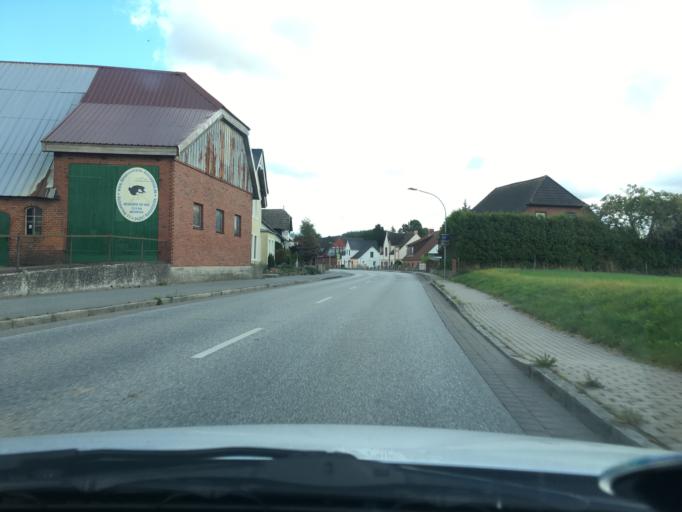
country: DE
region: Schleswig-Holstein
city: Barsbek
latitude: 54.4049
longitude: 10.3279
